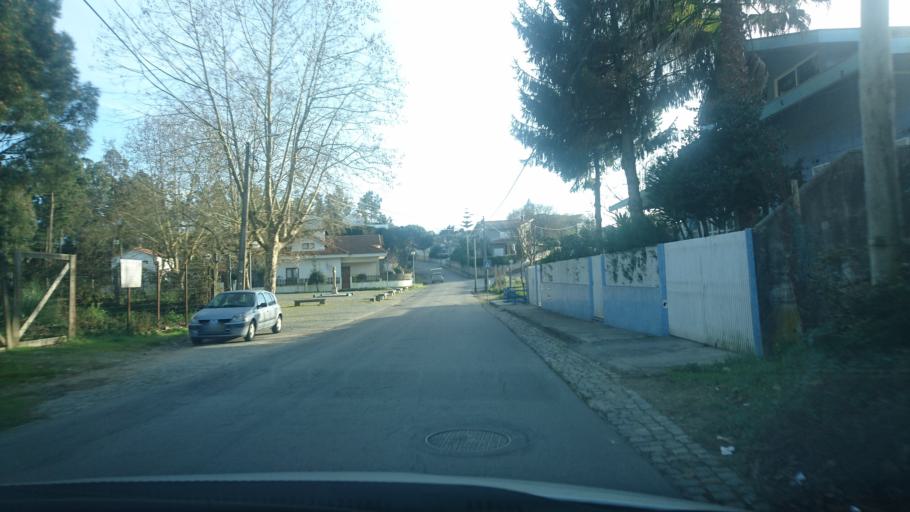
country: PT
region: Aveiro
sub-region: Santa Maria da Feira
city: Nogueira da Regedoura
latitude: 41.0027
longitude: -8.6057
